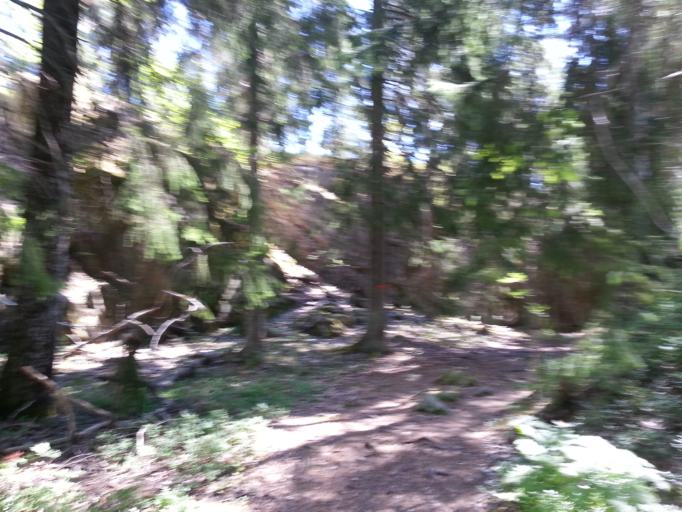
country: SE
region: Stockholm
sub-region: Tyreso Kommun
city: Bollmora
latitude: 59.2267
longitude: 18.2624
